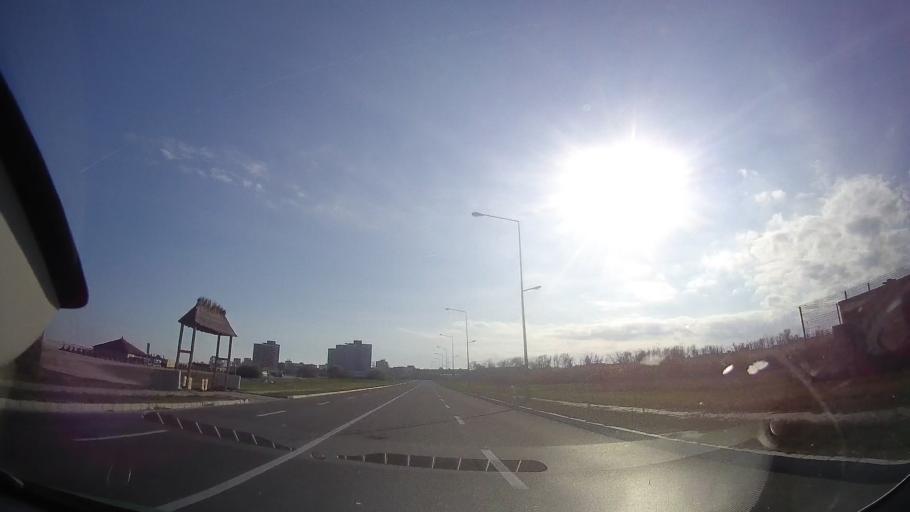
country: RO
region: Constanta
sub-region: Municipiul Mangalia
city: Mangalia
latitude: 43.8368
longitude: 28.5893
